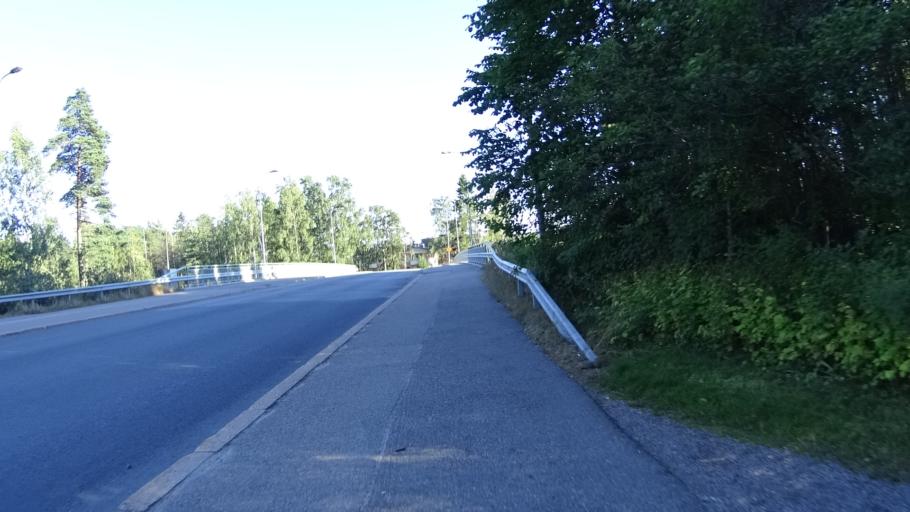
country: FI
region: Uusimaa
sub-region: Helsinki
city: Teekkarikylae
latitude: 60.2035
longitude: 24.8720
